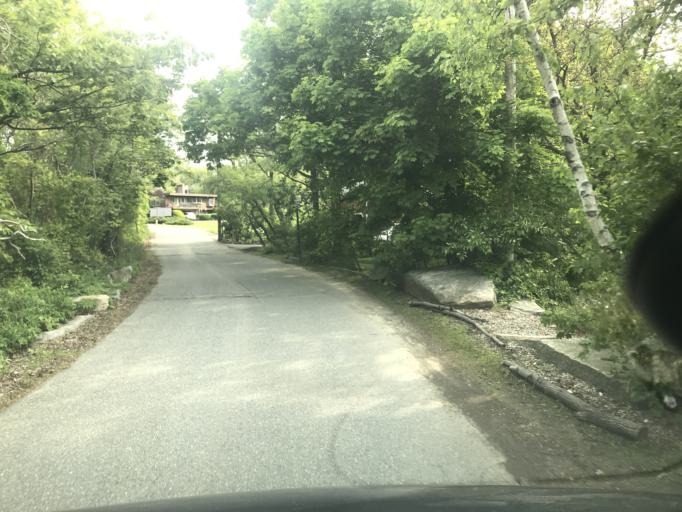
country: US
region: Massachusetts
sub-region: Essex County
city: Rockport
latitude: 42.6695
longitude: -70.6266
